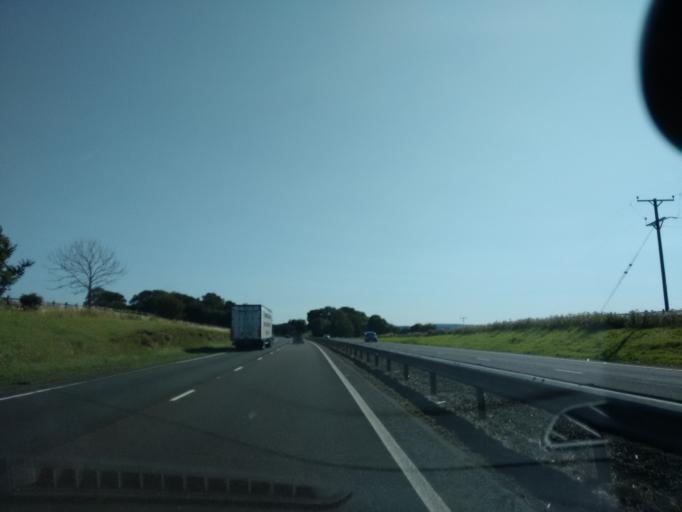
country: GB
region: England
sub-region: Northumberland
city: Corbridge
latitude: 54.9773
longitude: -1.9865
